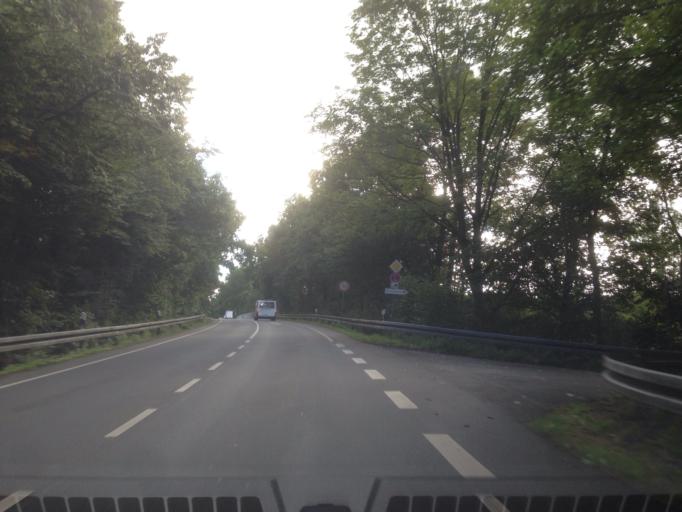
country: DE
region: North Rhine-Westphalia
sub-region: Regierungsbezirk Munster
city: Muenster
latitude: 51.9171
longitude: 7.5710
